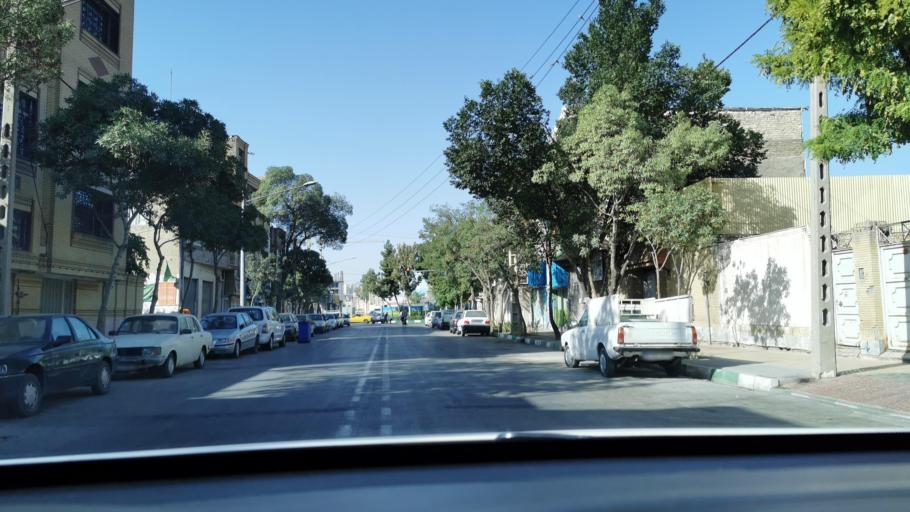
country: IR
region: Razavi Khorasan
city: Mashhad
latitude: 36.2994
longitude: 59.6202
